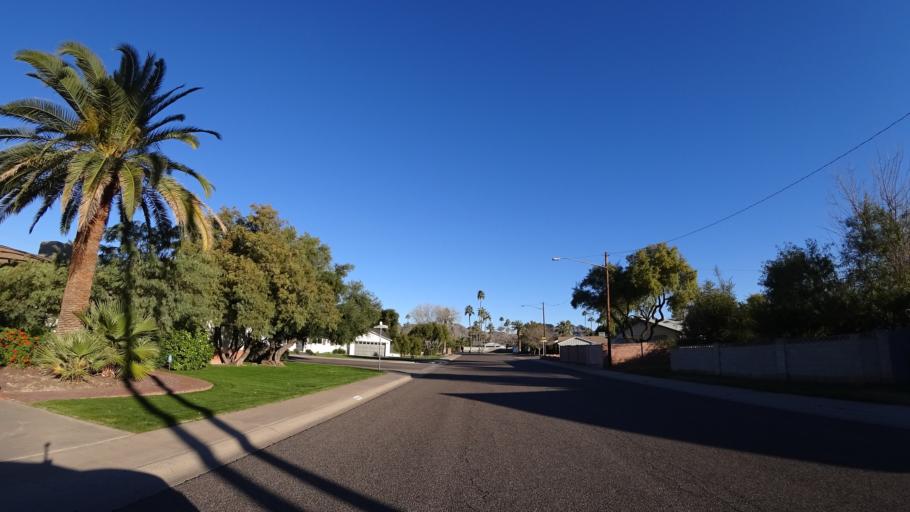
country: US
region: Arizona
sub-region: Maricopa County
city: Paradise Valley
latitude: 33.5083
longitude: -112.0080
